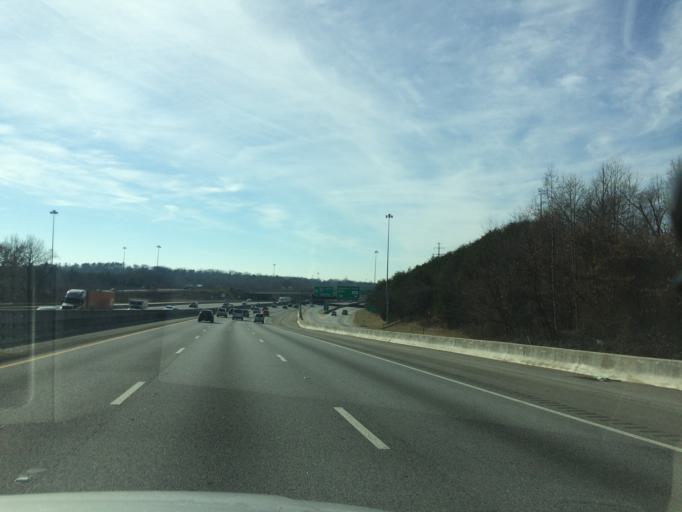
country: US
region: South Carolina
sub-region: Greenville County
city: Gantt
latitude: 34.7987
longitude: -82.3721
